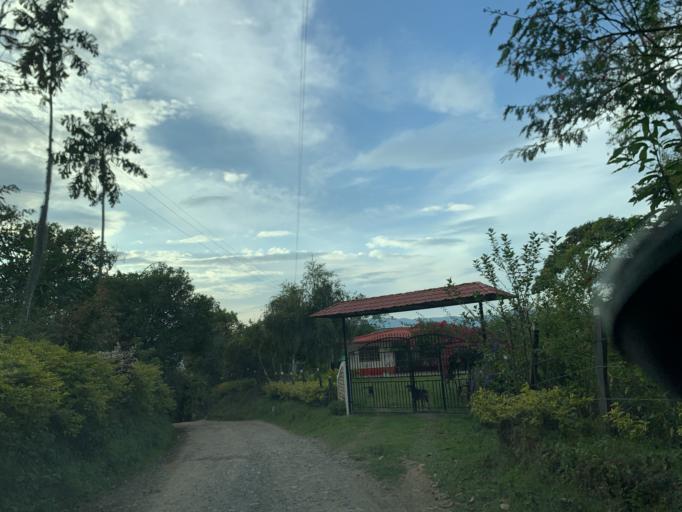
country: CO
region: Boyaca
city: Santana
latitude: 6.0786
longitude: -73.4883
